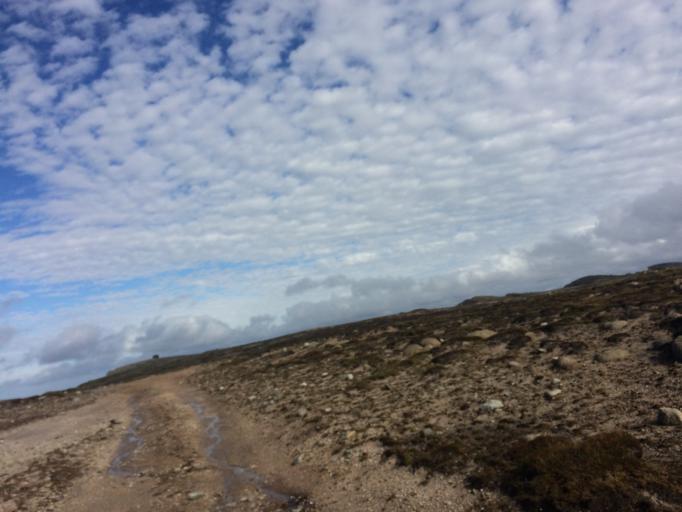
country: IE
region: Ulster
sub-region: County Donegal
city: Derrybeg
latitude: 55.2701
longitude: -8.2471
